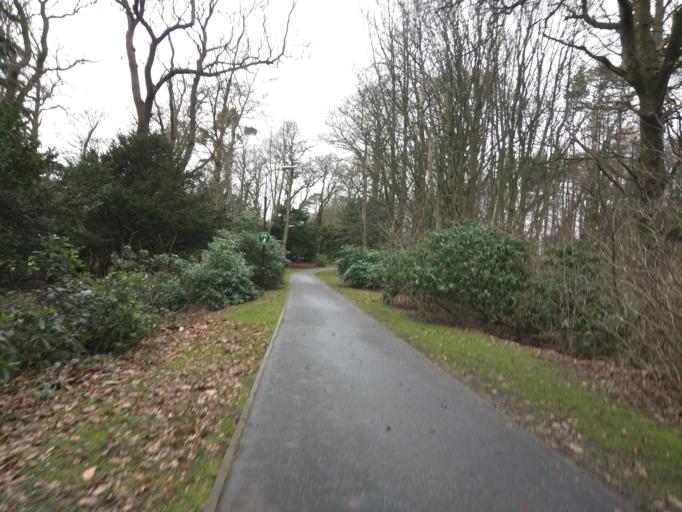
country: GB
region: Scotland
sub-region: Edinburgh
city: Currie
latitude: 55.9150
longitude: -3.3200
